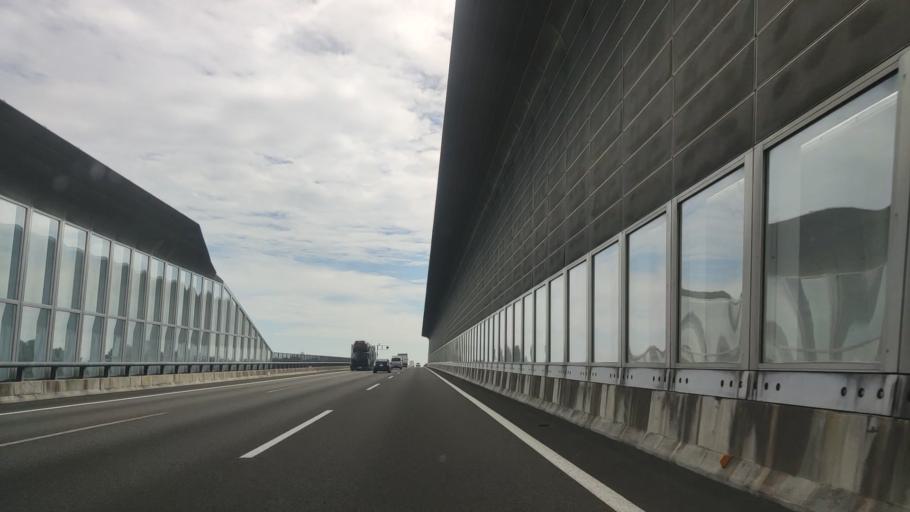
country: JP
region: Aichi
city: Chiryu
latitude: 35.0270
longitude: 137.0652
